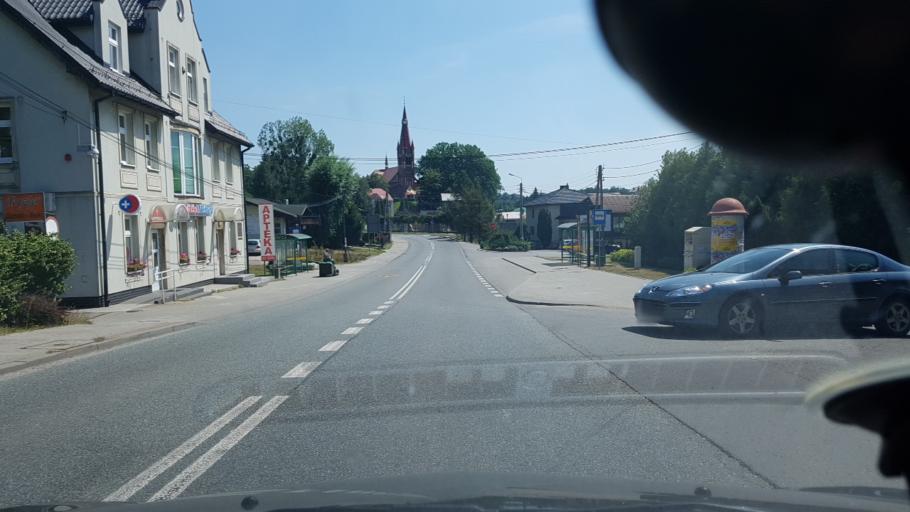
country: PL
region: Silesian Voivodeship
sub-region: Powiat wodzislawski
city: Marklowice
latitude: 50.0184
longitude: 18.5134
